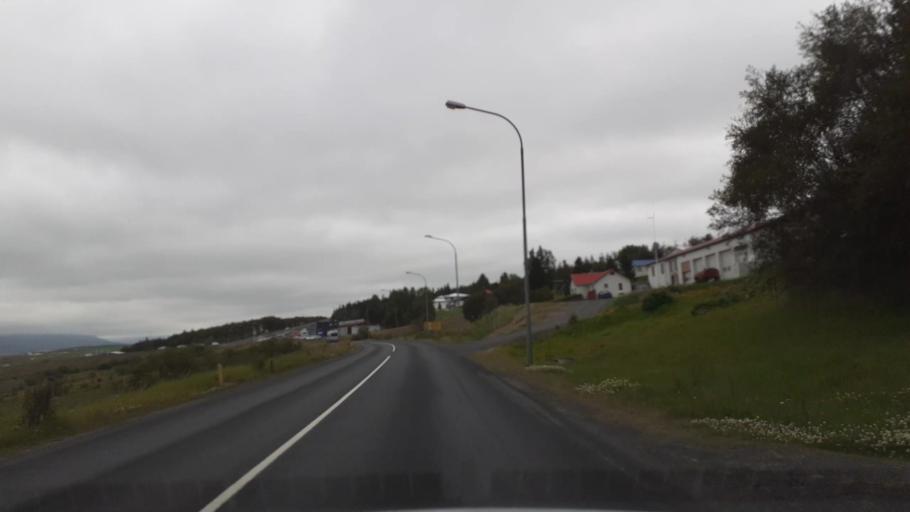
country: IS
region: Northwest
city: Saudarkrokur
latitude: 65.5562
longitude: -19.4505
